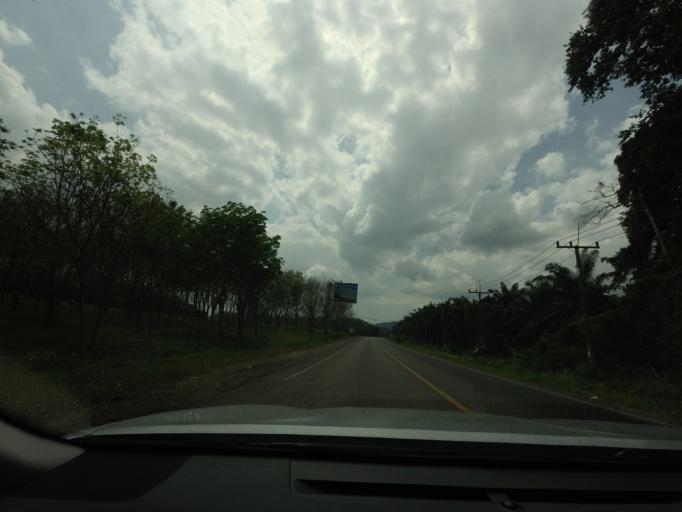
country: TH
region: Phangnga
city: Ban Ao Nang
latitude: 8.1286
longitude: 98.8063
